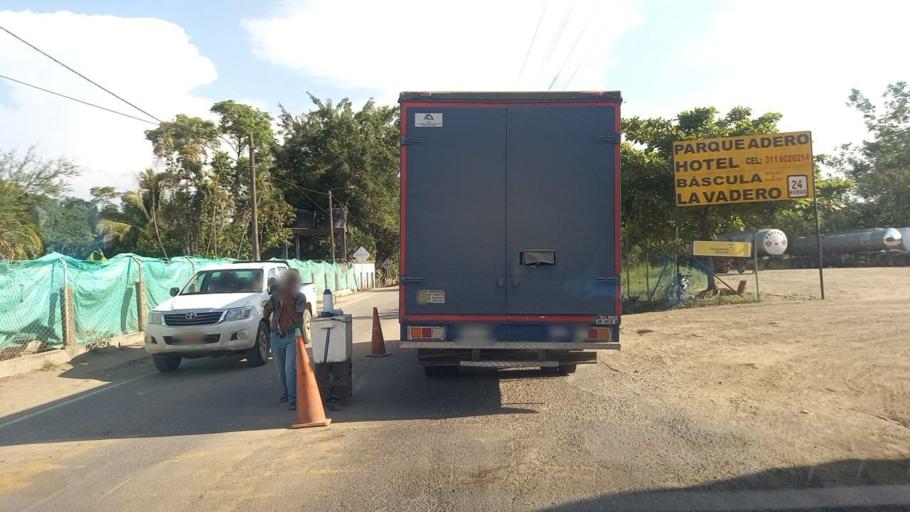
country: CO
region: Boyaca
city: Puerto Boyaca
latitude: 5.9387
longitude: -74.5705
